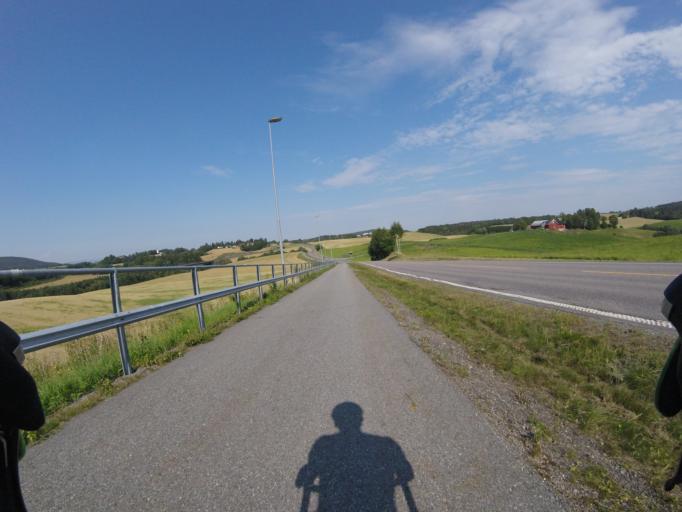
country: NO
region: Akershus
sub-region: Sorum
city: Frogner
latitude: 60.0082
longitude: 11.1072
